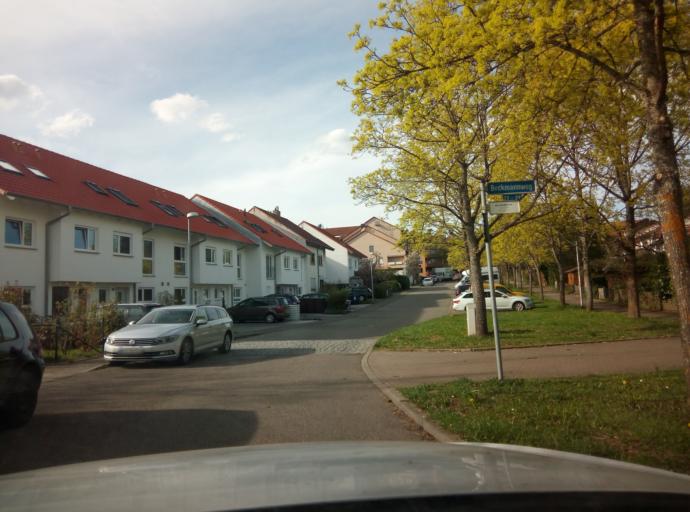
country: DE
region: Baden-Wuerttemberg
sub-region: Tuebingen Region
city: Tuebingen
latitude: 48.5376
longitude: 9.0443
